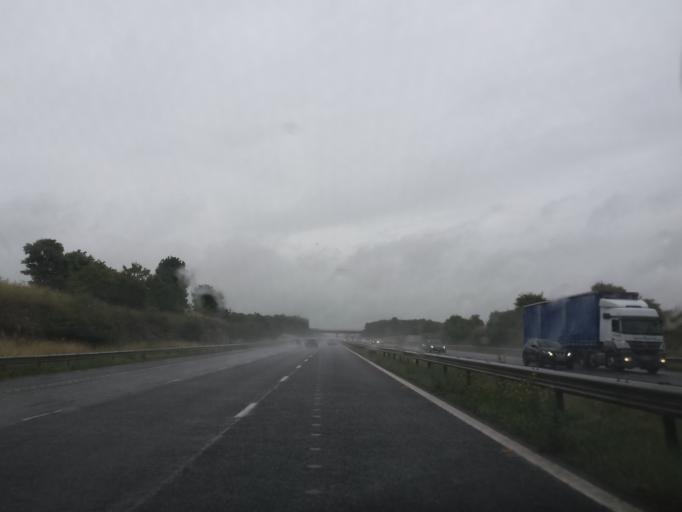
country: GB
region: England
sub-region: Doncaster
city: Stainton
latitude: 53.4635
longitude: -1.1880
